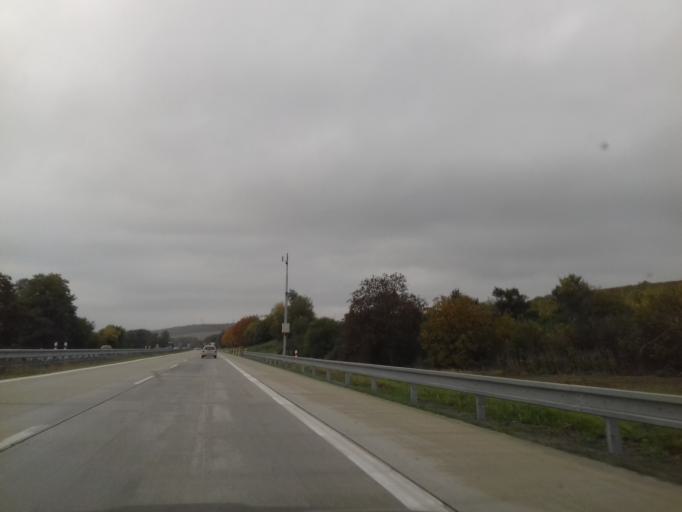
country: CZ
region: South Moravian
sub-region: Okres Breclav
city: Hustopece
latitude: 48.9196
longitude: 16.7686
